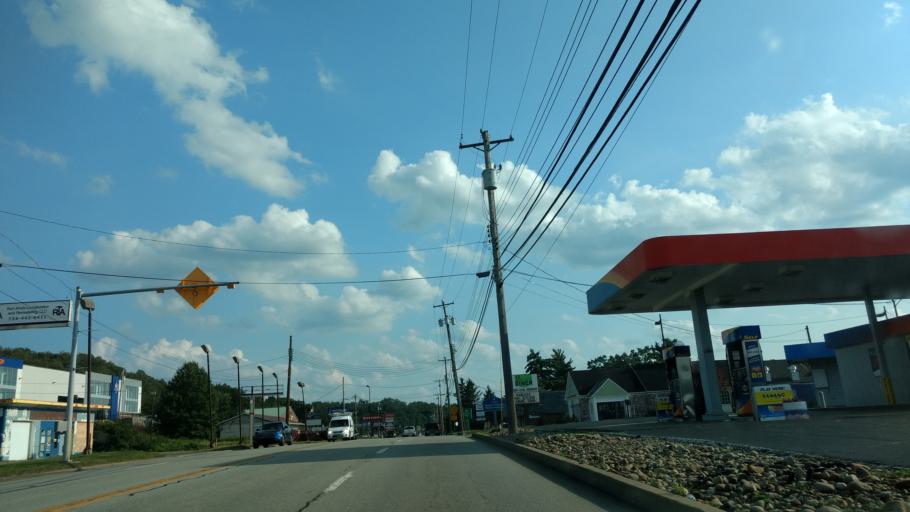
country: US
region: Pennsylvania
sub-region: Allegheny County
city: Gibsonia
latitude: 40.5975
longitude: -79.9477
